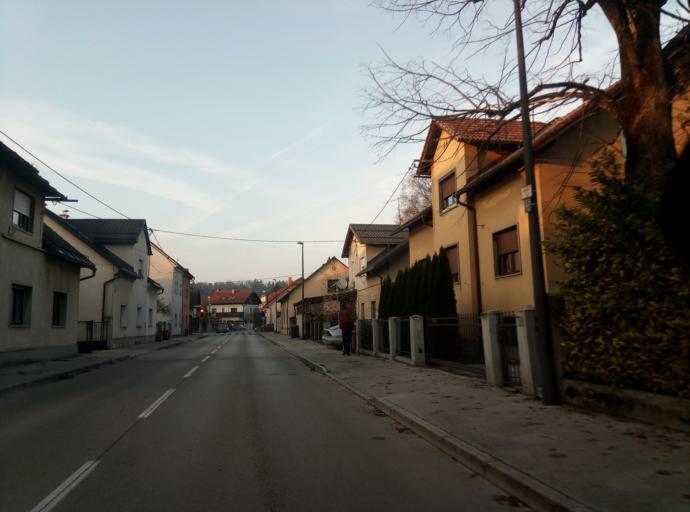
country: SI
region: Ljubljana
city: Ljubljana
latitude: 46.0480
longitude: 14.4856
